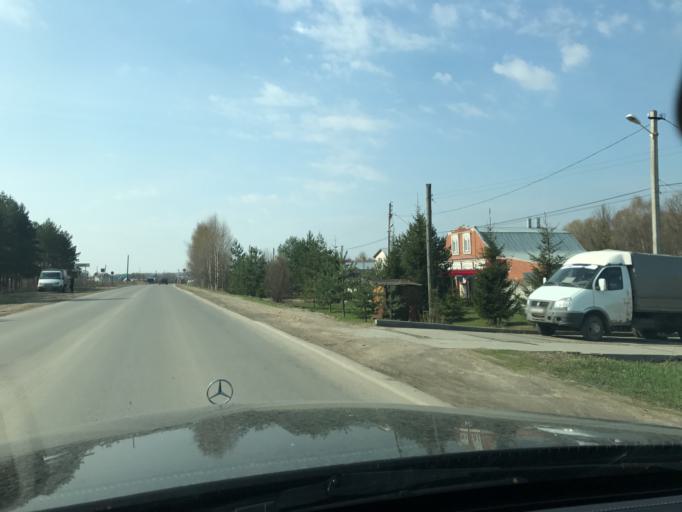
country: RU
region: Nizjnij Novgorod
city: Taremskoye
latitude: 55.9366
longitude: 43.0462
